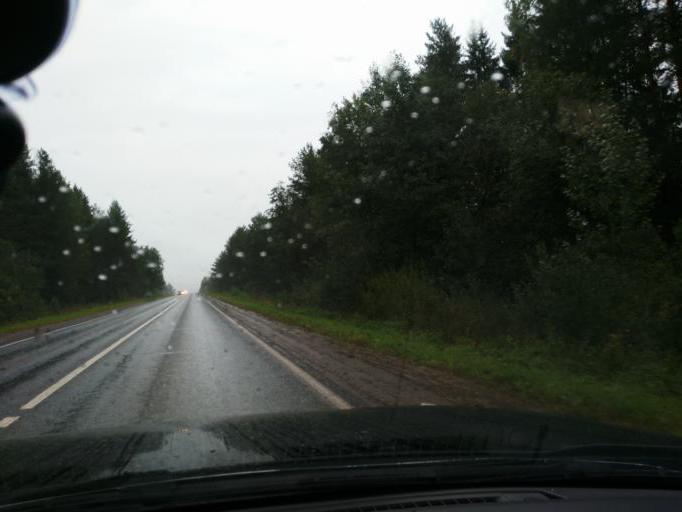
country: RU
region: Perm
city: Yugo-Kamskiy
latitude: 57.5649
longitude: 55.6795
